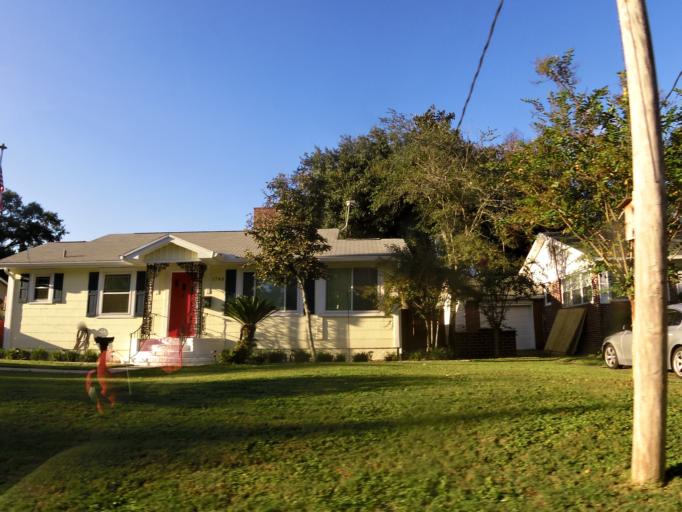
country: US
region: Florida
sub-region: Duval County
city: Jacksonville
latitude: 30.2825
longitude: -81.6481
